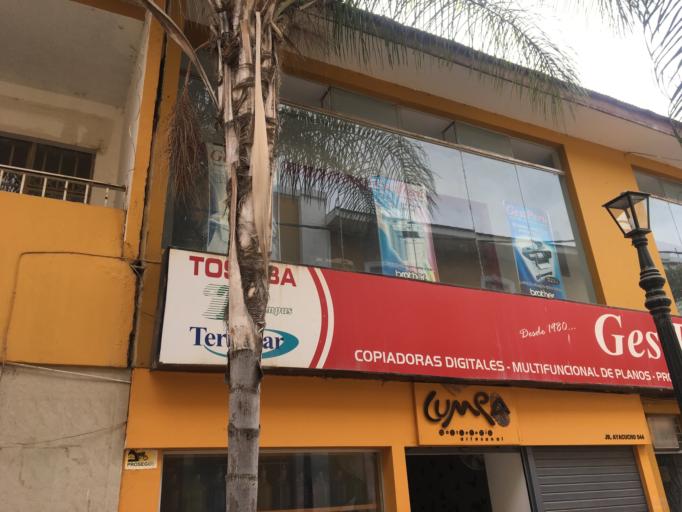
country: PE
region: Piura
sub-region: Provincia de Piura
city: Piura
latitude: -5.1972
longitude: -80.6282
